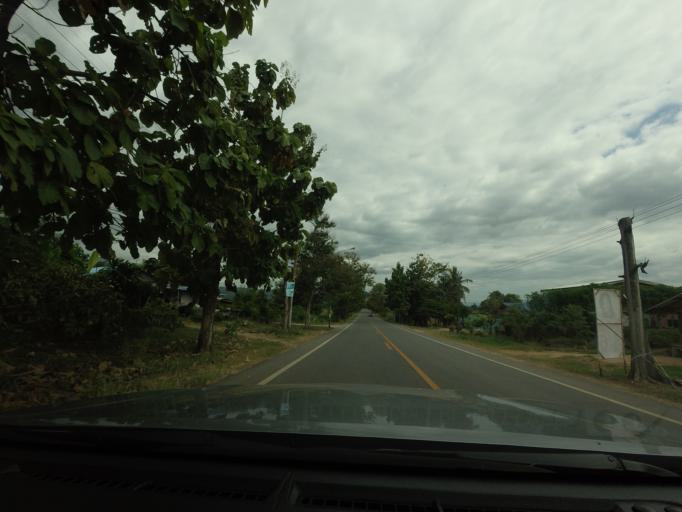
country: TH
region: Phitsanulok
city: Noen Maprang
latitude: 16.6918
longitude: 100.5469
